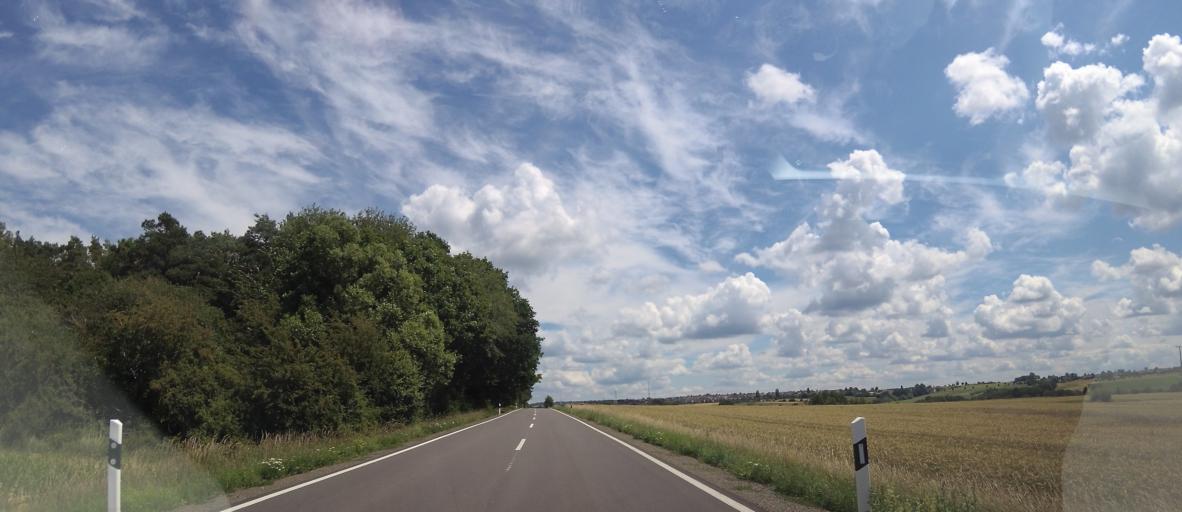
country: DE
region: Rheinland-Pfalz
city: Kroppen
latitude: 49.1664
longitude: 7.5258
